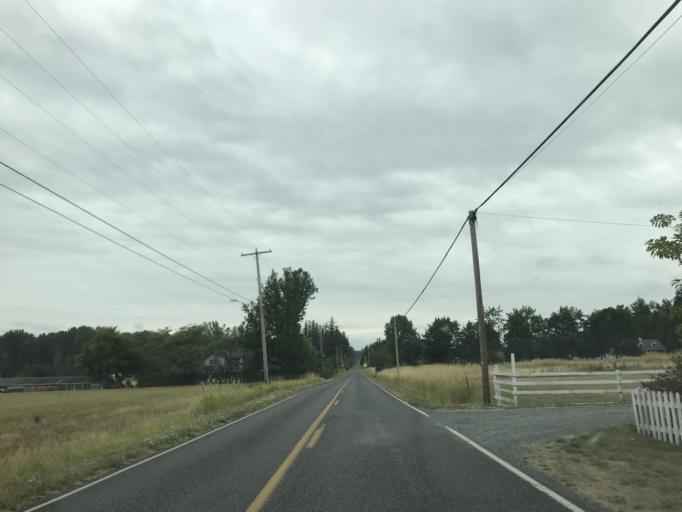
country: US
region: Washington
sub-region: Whatcom County
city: Sudden Valley
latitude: 48.8189
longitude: -122.3325
